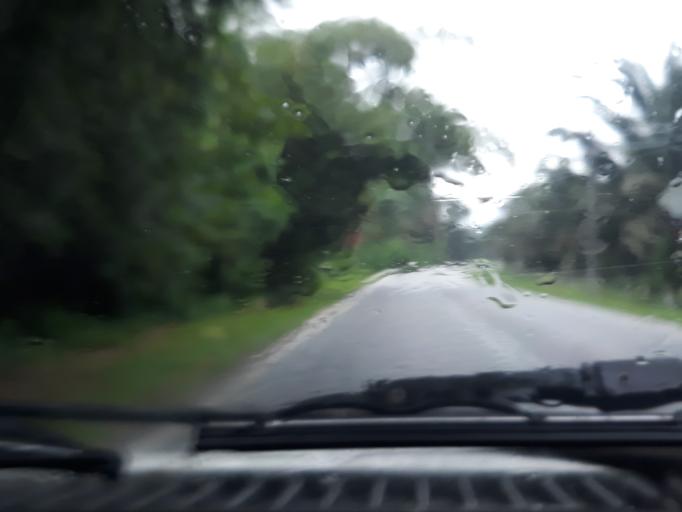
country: MY
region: Kedah
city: Kulim
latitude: 5.2500
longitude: 100.6032
